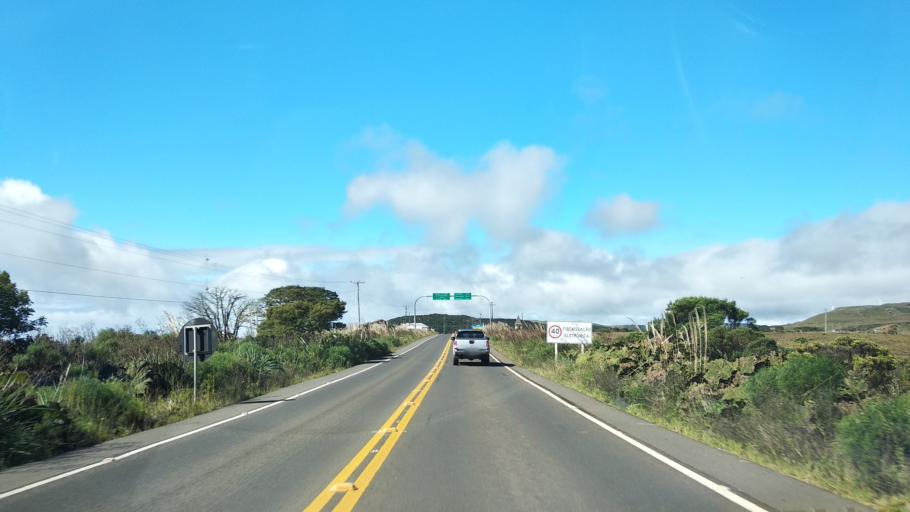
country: BR
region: Santa Catarina
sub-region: Lauro Muller
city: Lauro Muller
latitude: -28.3908
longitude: -49.5514
